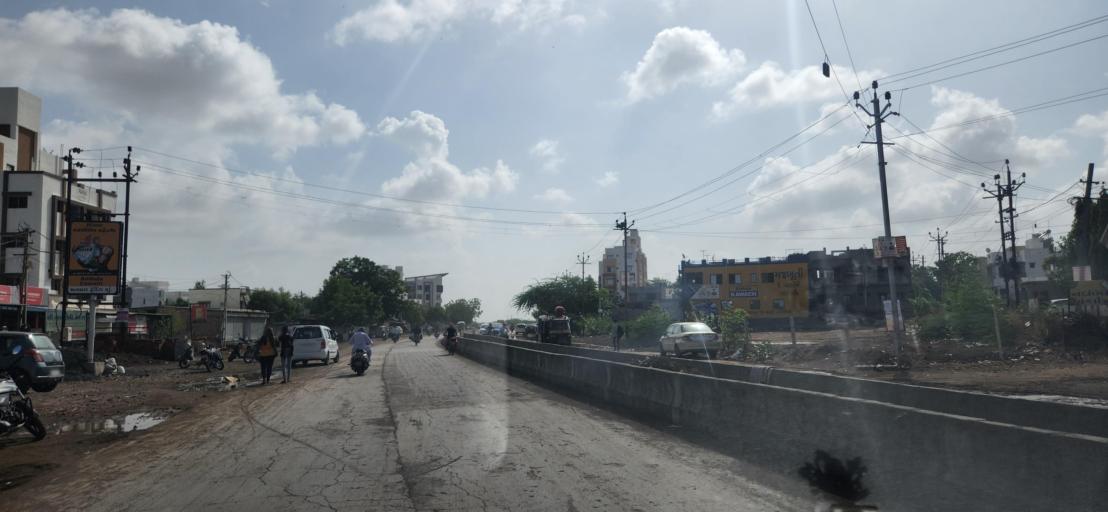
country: IN
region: Gujarat
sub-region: Bhavnagar
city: Bhavnagar
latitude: 21.7330
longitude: 72.1542
